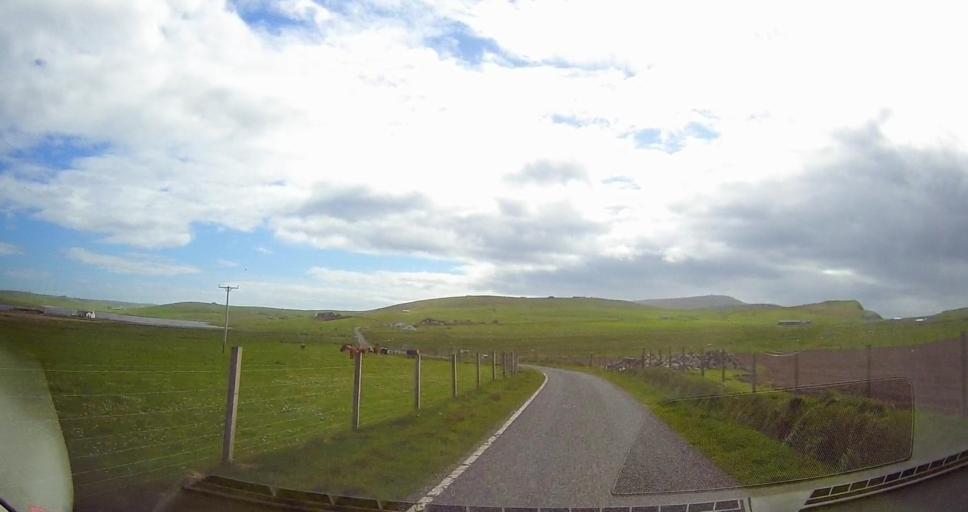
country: GB
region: Scotland
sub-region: Shetland Islands
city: Sandwick
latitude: 59.9388
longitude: -1.3461
